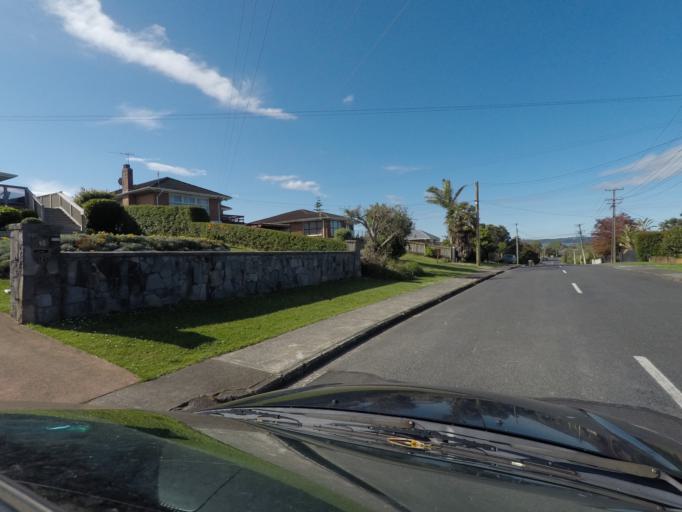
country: NZ
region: Auckland
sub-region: Auckland
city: Rosebank
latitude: -36.8686
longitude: 174.6495
